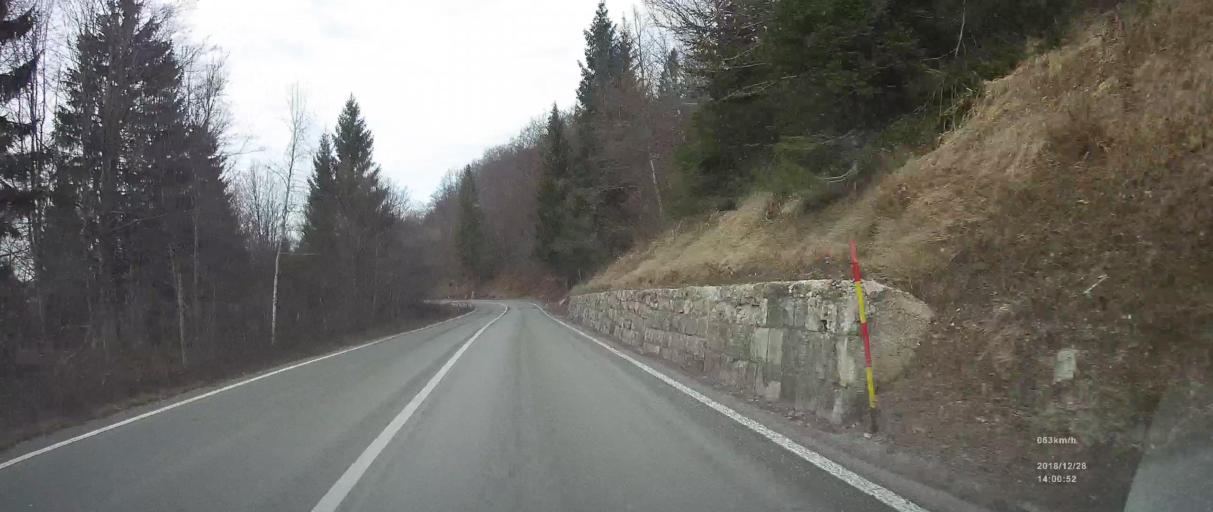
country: SI
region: Kostel
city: Kostel
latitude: 45.4153
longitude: 14.9122
